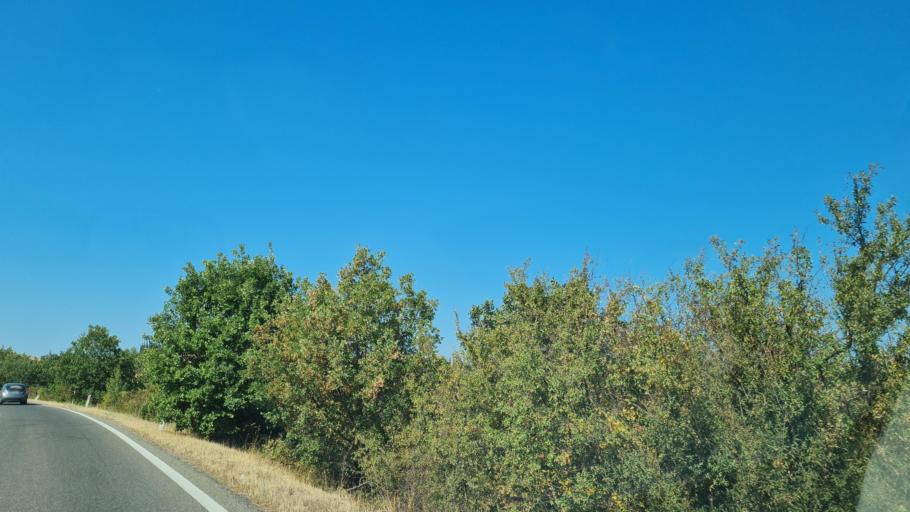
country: IT
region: Tuscany
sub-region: Provincia di Siena
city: Chianciano Terme
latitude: 43.0070
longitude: 11.7326
